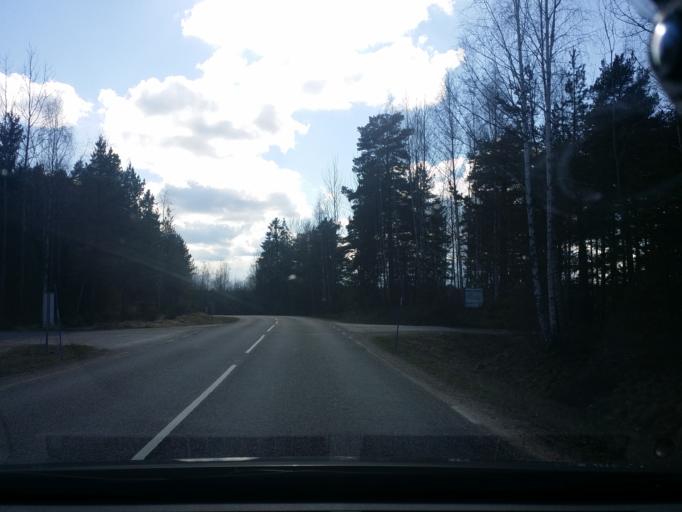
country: SE
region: Vaestmanland
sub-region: Sala Kommun
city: Sala
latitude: 59.9904
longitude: 16.4786
